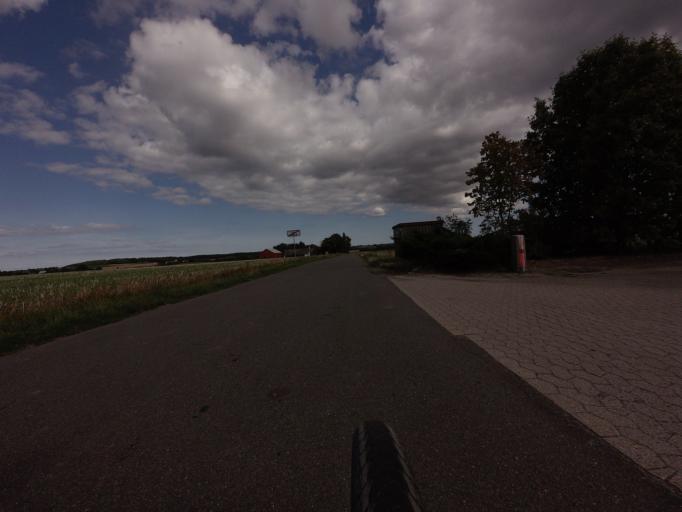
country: DK
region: Zealand
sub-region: Vordingborg Kommune
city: Stege
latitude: 55.0044
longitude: 12.3178
